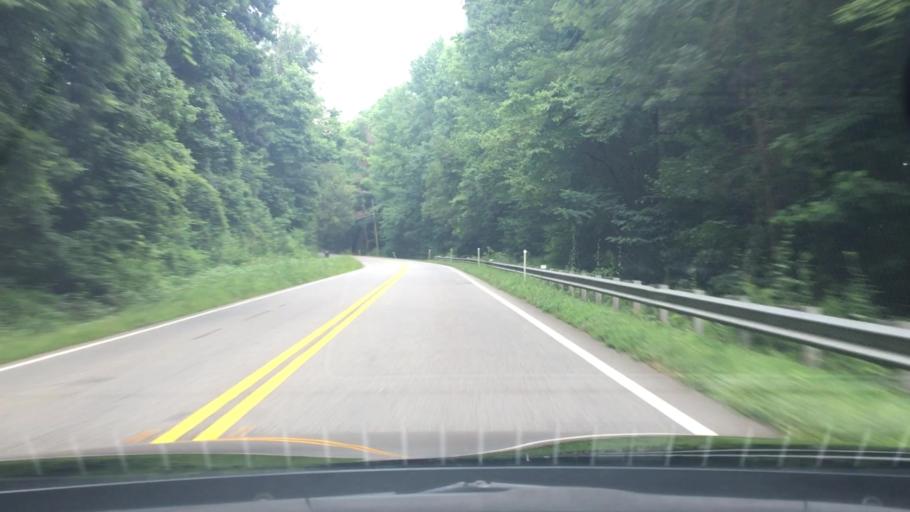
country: US
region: Georgia
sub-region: Coweta County
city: East Newnan
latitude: 33.3765
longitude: -84.7273
